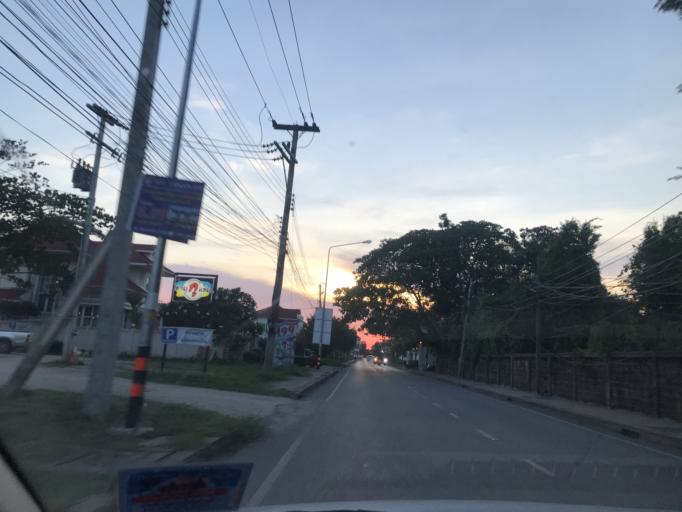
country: TH
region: Changwat Udon Thani
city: Udon Thani
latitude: 17.4009
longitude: 102.7767
